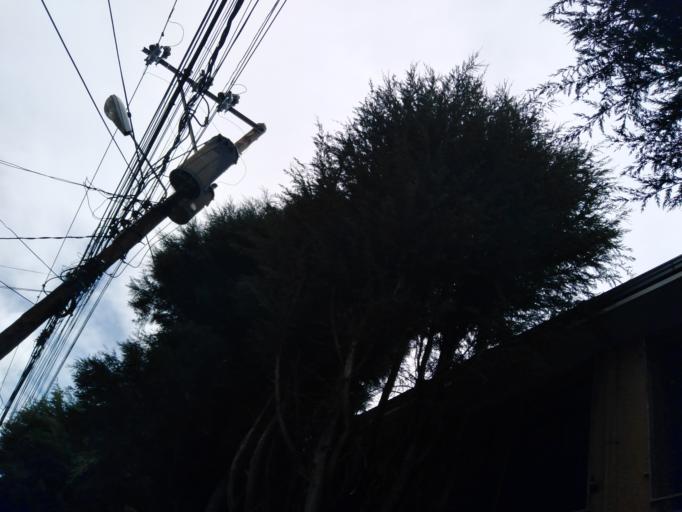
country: BO
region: La Paz
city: La Paz
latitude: -16.5134
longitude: -68.1348
